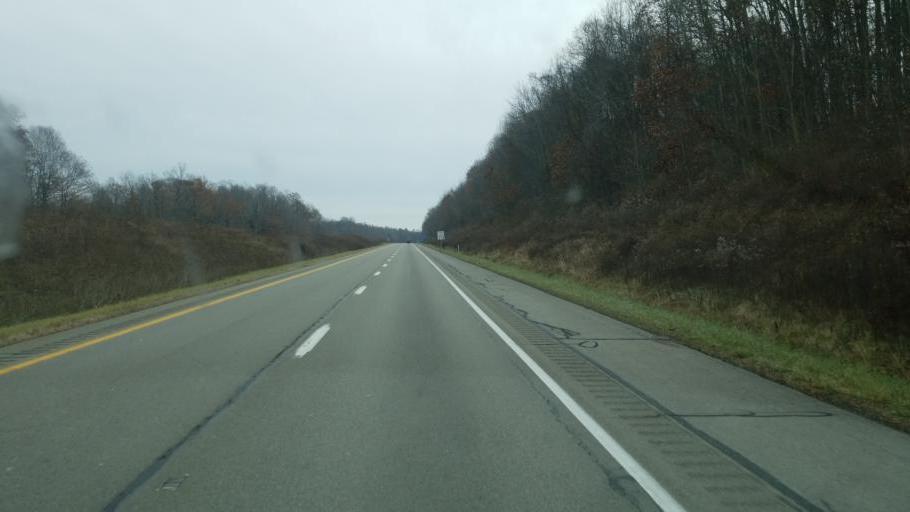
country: US
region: Pennsylvania
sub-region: Crawford County
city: Meadville
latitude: 41.5326
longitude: -80.1778
